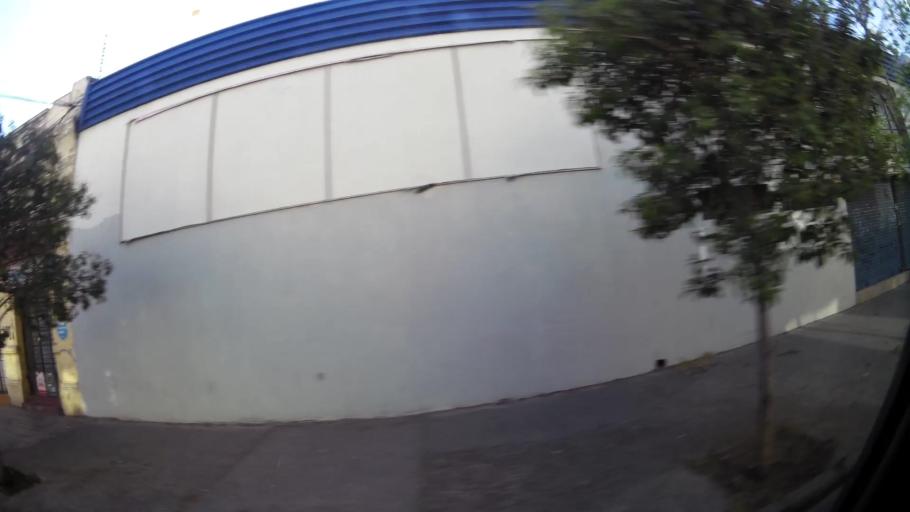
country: CL
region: Santiago Metropolitan
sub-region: Provincia de Santiago
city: Santiago
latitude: -33.4575
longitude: -70.6476
